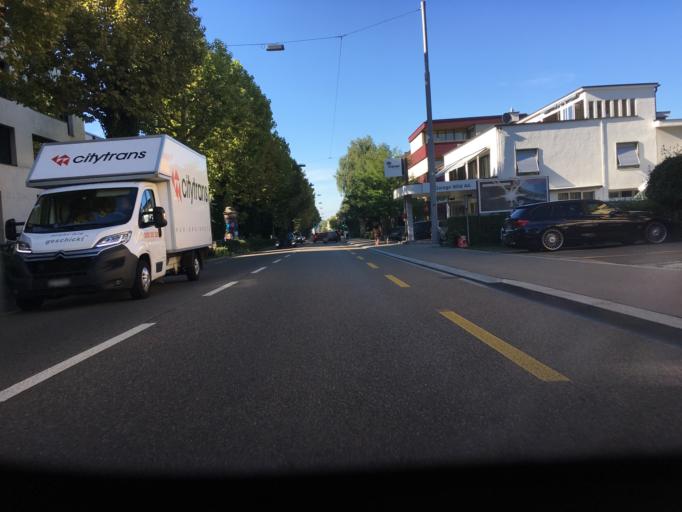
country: CH
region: Zurich
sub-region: Bezirk Zuerich
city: Zuerich (Kreis 2) / Wollishofen
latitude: 47.3351
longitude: 8.5301
